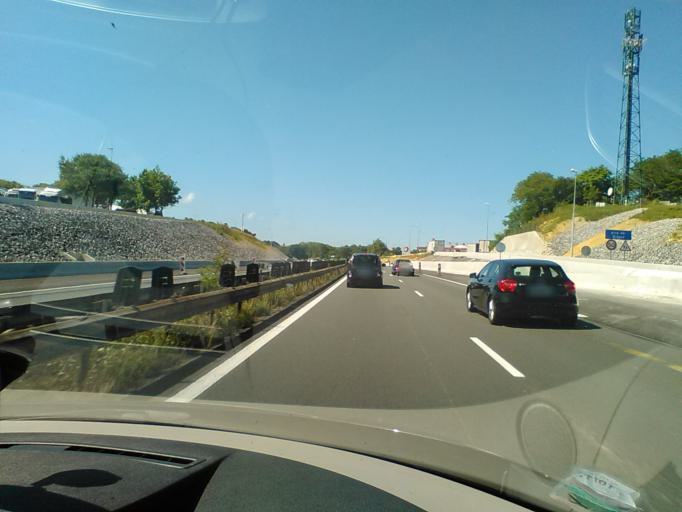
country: FR
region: Aquitaine
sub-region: Departement des Pyrenees-Atlantiques
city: Bidart
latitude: 43.4241
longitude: -1.5957
